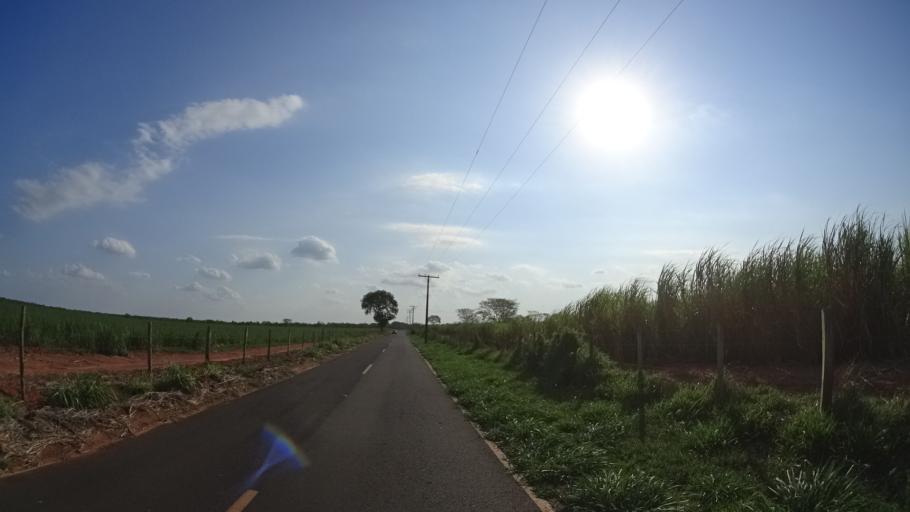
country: BR
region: Sao Paulo
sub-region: Urupes
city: Urupes
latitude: -21.3900
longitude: -49.5027
